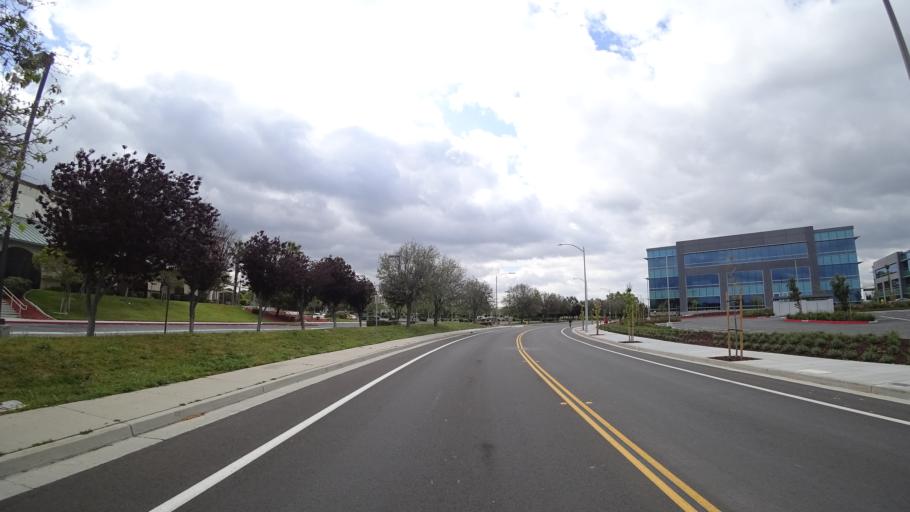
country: US
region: California
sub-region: Santa Clara County
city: Milpitas
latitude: 37.4255
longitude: -121.9609
